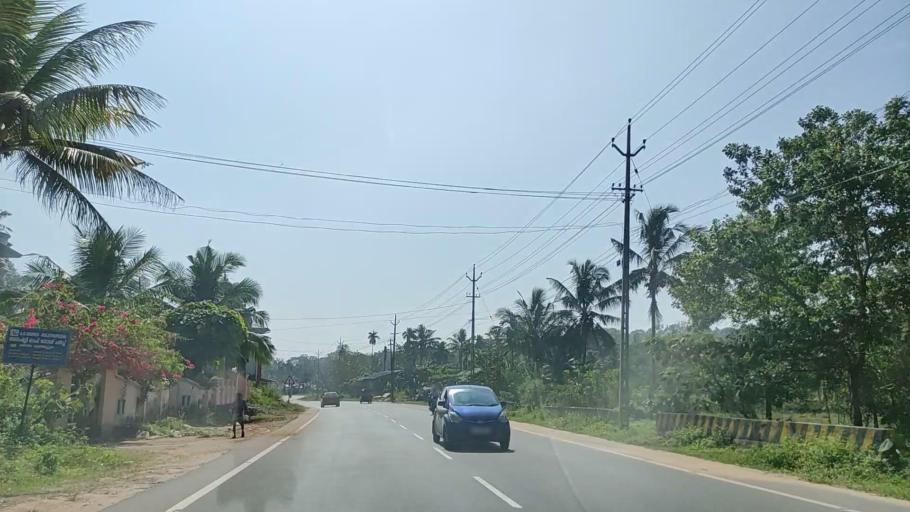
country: IN
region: Kerala
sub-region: Kollam
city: Punalur
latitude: 8.9116
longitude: 77.0476
